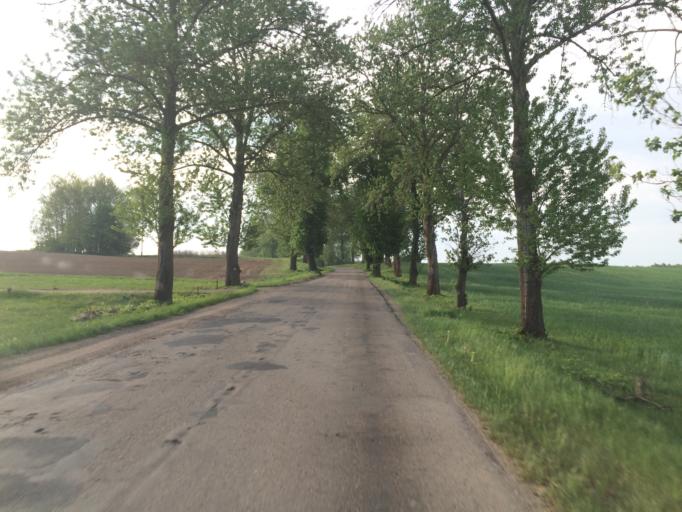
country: PL
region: Warmian-Masurian Voivodeship
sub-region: Powiat dzialdowski
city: Rybno
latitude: 53.3326
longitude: 20.0071
